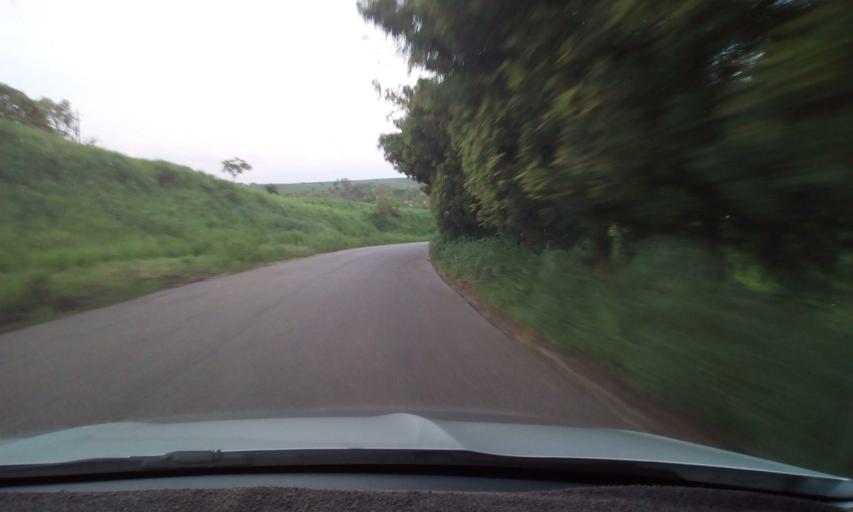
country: BR
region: Pernambuco
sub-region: Condado
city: Condado
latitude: -7.5982
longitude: -35.2184
